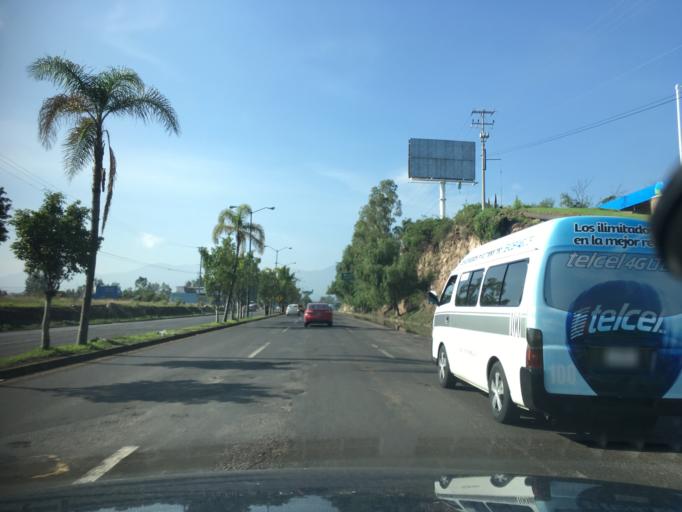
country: MX
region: Michoacan
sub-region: Morelia
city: San Antonio
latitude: 19.6901
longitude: -101.2393
